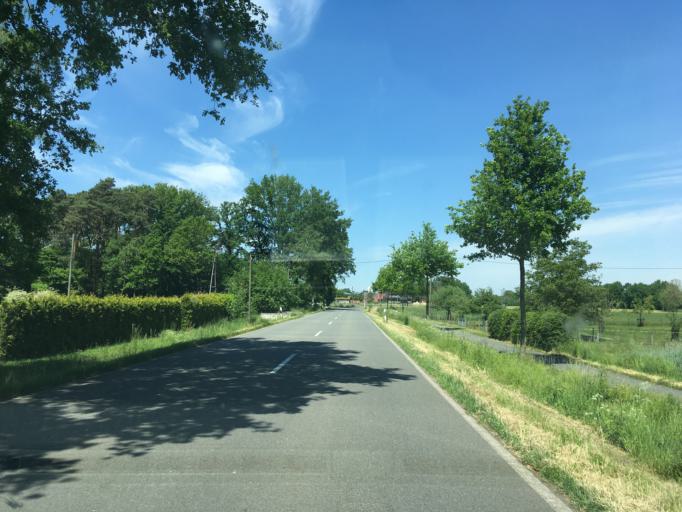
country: DE
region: North Rhine-Westphalia
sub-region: Regierungsbezirk Munster
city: Borken
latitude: 51.8704
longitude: 6.8319
